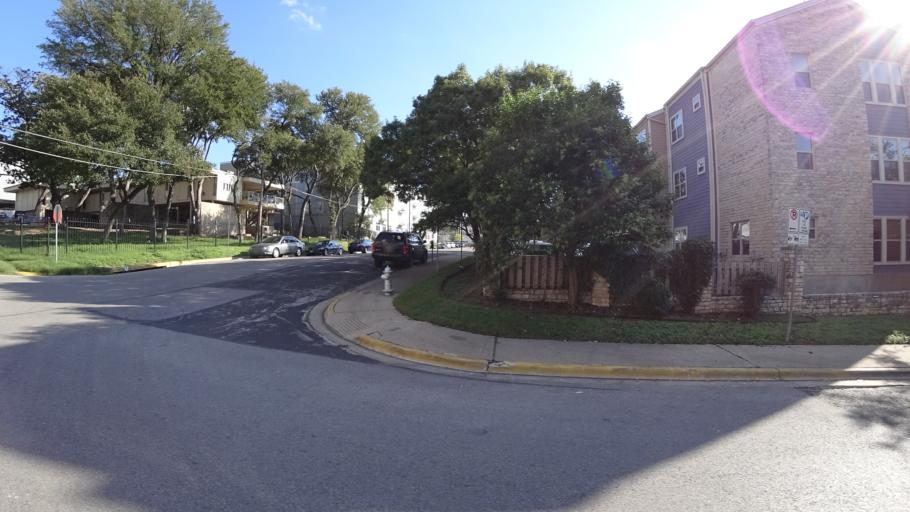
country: US
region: Texas
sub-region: Travis County
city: Austin
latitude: 30.2897
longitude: -97.7508
